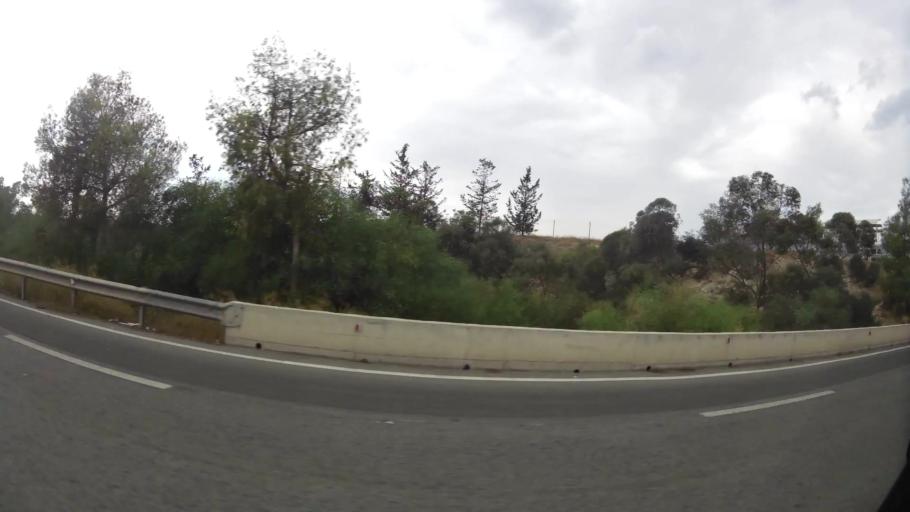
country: CY
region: Lefkosia
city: Nicosia
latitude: 35.1368
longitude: 33.3745
